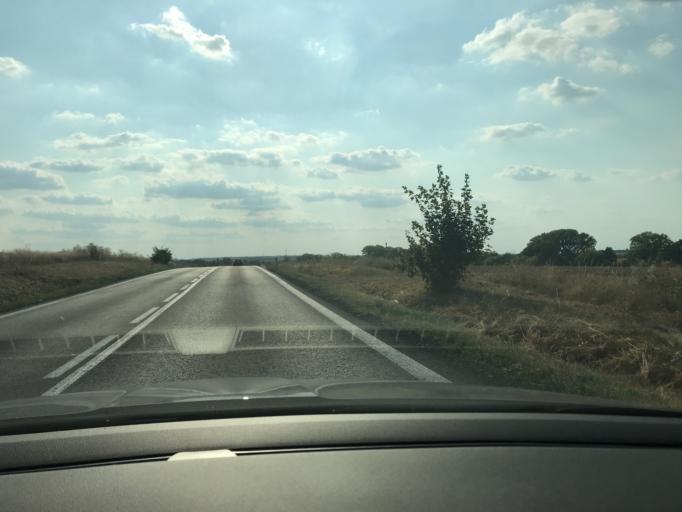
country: CZ
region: Central Bohemia
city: Velvary
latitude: 50.2691
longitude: 14.2128
